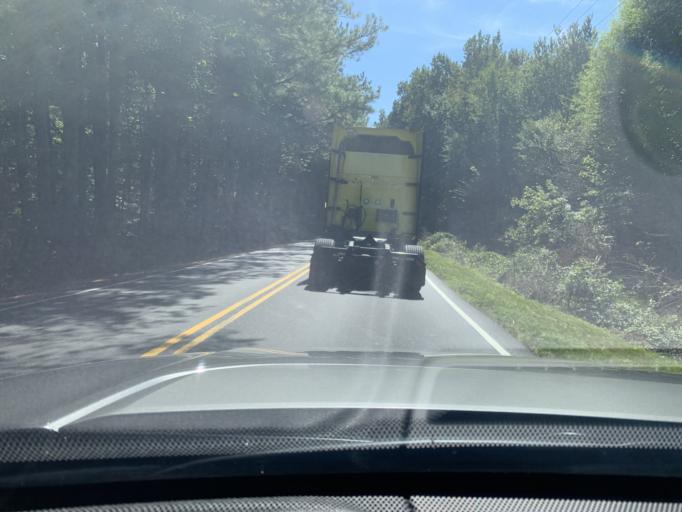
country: US
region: Georgia
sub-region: Clayton County
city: Conley
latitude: 33.6685
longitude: -84.3318
